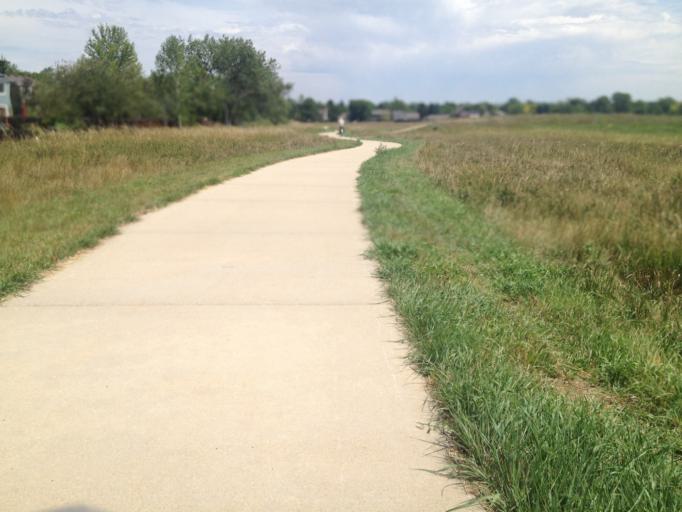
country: US
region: Colorado
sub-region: Boulder County
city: Louisville
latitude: 39.9723
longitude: -105.1453
